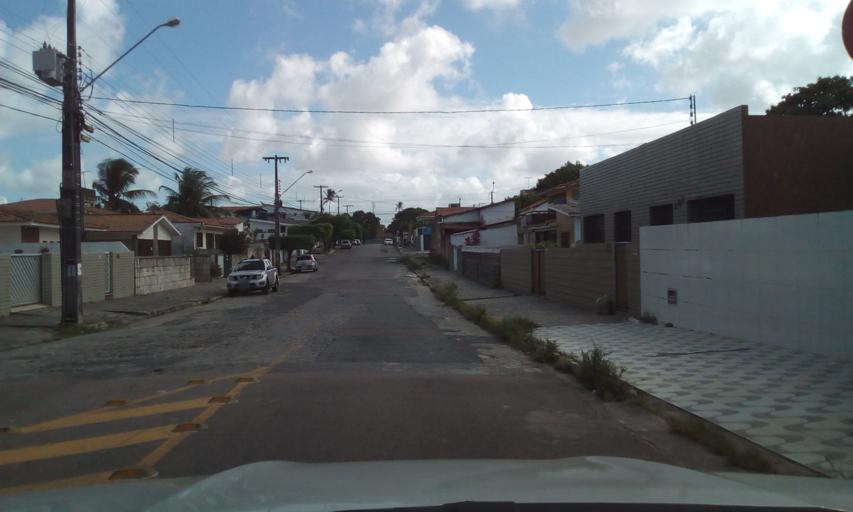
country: BR
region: Paraiba
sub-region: Joao Pessoa
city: Joao Pessoa
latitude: -7.1370
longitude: -34.8806
